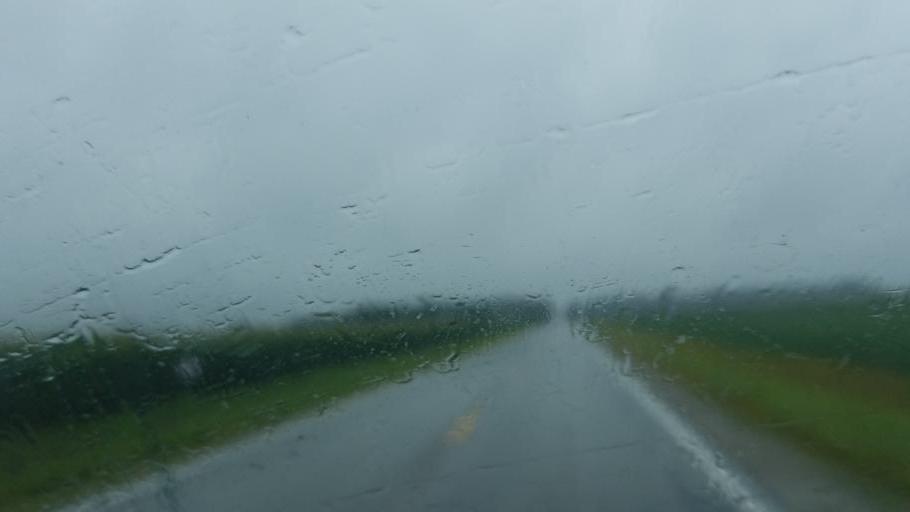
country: US
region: Indiana
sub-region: Huntington County
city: Warren
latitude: 40.6548
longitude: -85.3503
